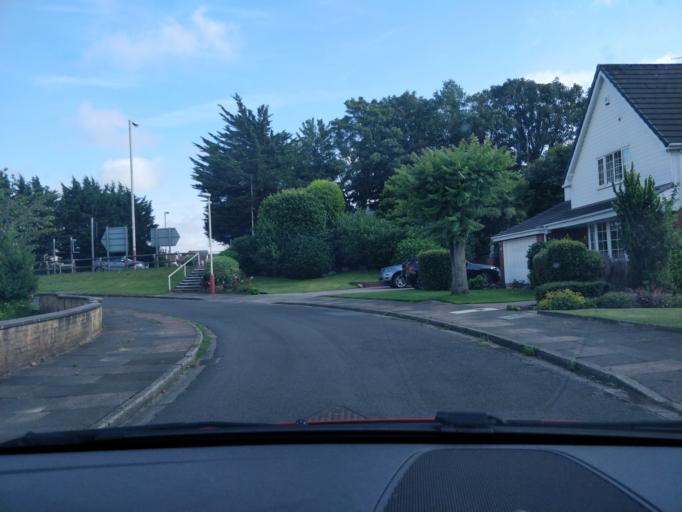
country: GB
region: England
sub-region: Sefton
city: Southport
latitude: 53.6525
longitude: -2.9798
